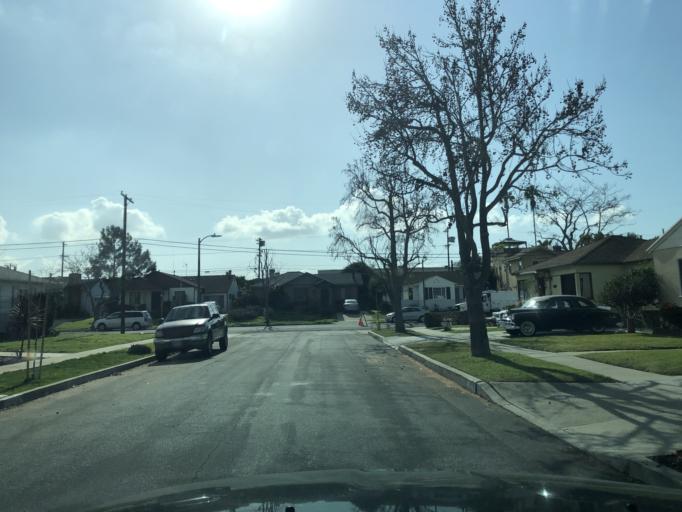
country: US
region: California
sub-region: Los Angeles County
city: Inglewood
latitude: 33.9645
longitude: -118.3745
